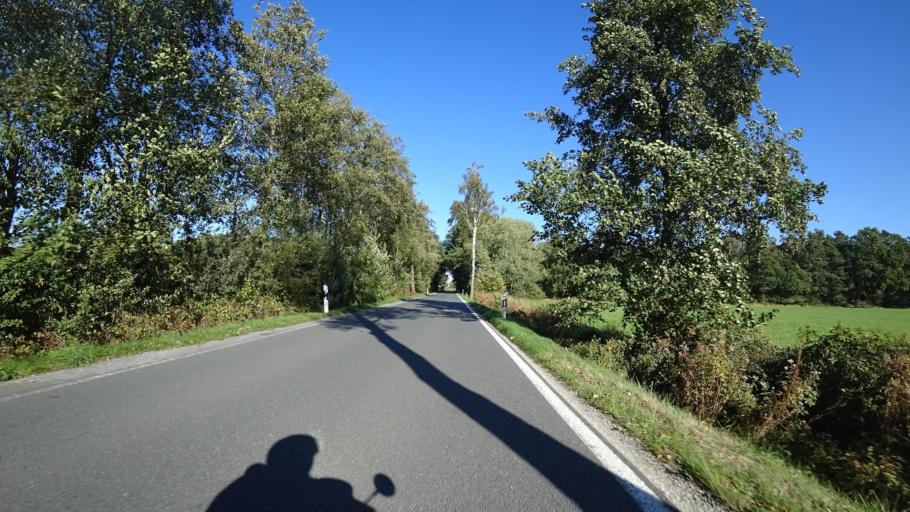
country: DE
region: North Rhine-Westphalia
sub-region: Regierungsbezirk Detmold
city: Guetersloh
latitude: 51.8730
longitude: 8.3857
